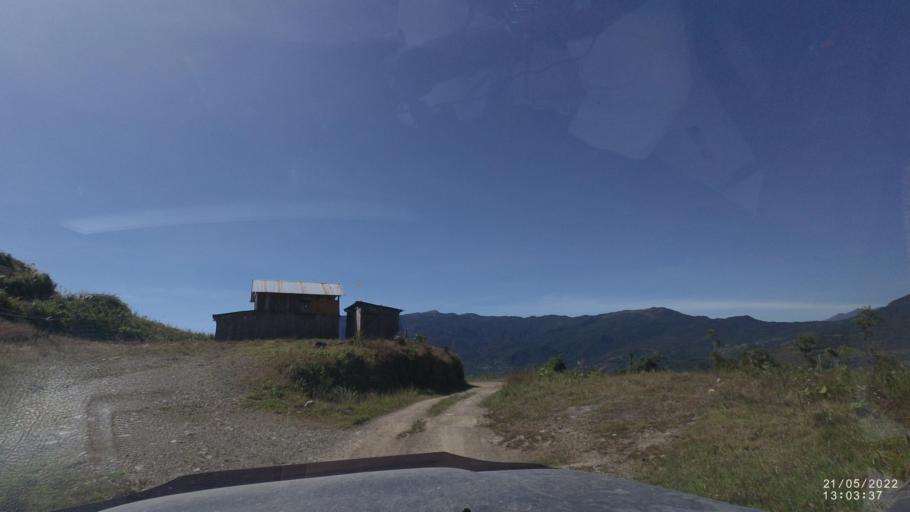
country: BO
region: Cochabamba
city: Colomi
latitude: -17.1584
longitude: -65.9523
